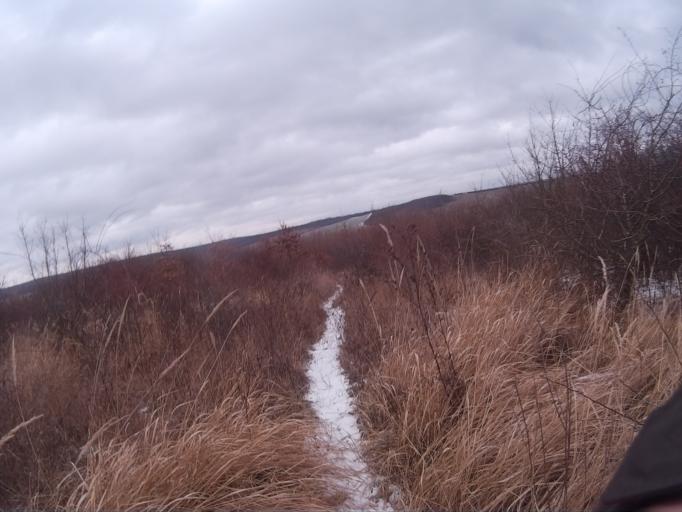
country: HU
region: Borsod-Abauj-Zemplen
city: Halmaj
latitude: 48.3719
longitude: 20.9663
